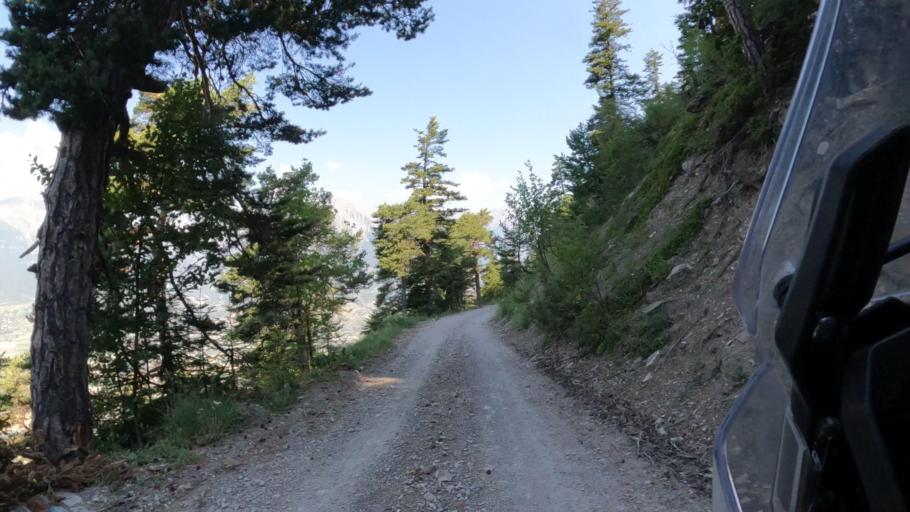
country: FR
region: Provence-Alpes-Cote d'Azur
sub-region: Departement des Hautes-Alpes
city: Embrun
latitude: 44.5938
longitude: 6.5652
